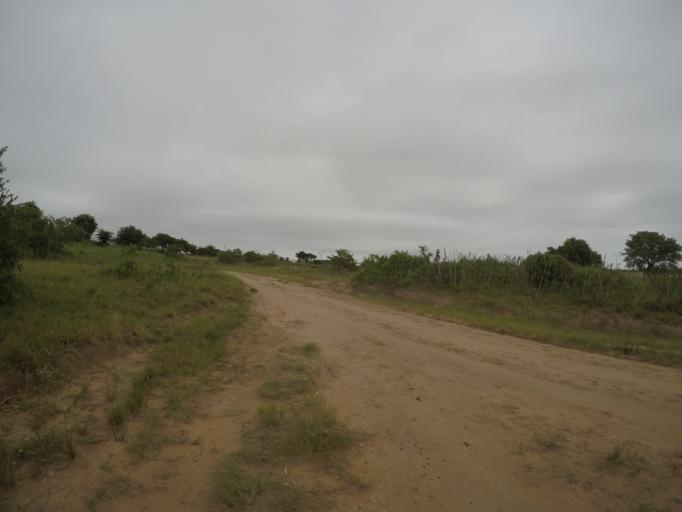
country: ZA
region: KwaZulu-Natal
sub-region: uThungulu District Municipality
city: Empangeni
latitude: -28.6123
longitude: 31.8387
